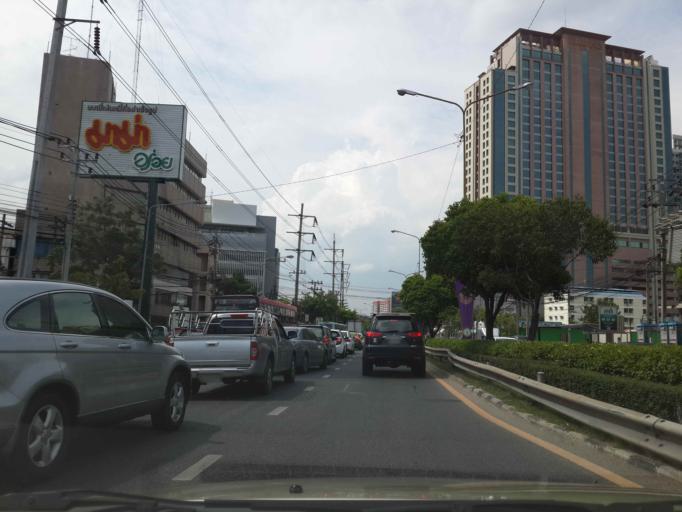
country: TH
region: Bangkok
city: Bang Kapi
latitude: 13.7522
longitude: 100.6453
